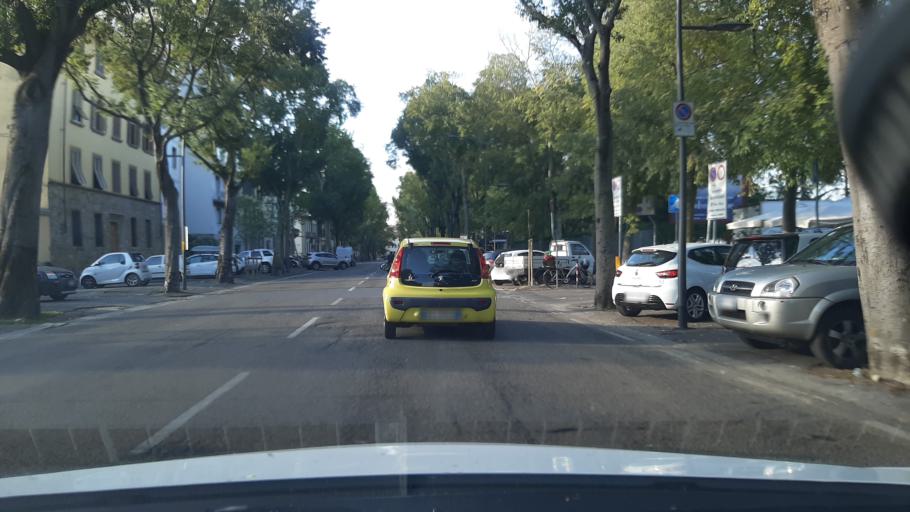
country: IT
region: Tuscany
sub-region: Province of Florence
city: Fiesole
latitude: 43.7769
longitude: 11.2862
